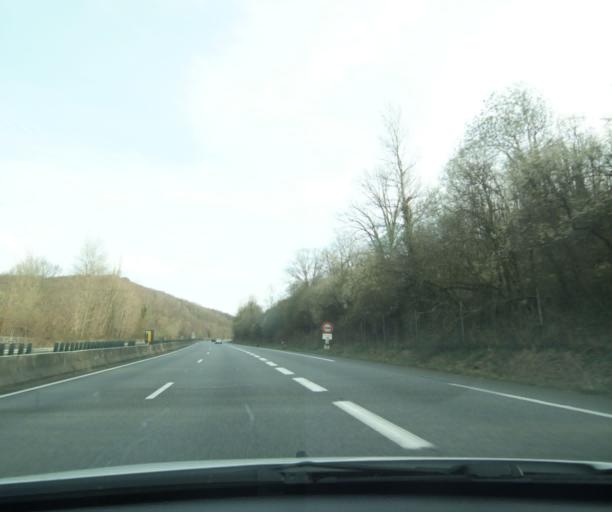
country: FR
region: Midi-Pyrenees
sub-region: Departement des Hautes-Pyrenees
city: Tournay
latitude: 43.1579
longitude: 0.2869
